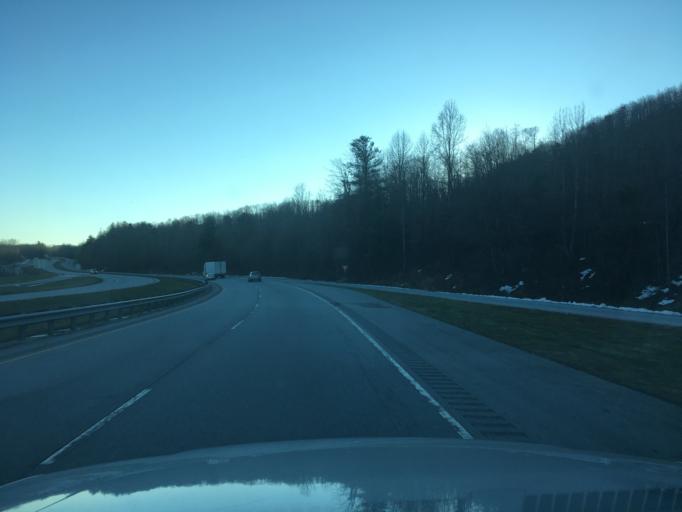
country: US
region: North Carolina
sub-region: Henderson County
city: East Flat Rock
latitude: 35.2580
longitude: -82.4085
